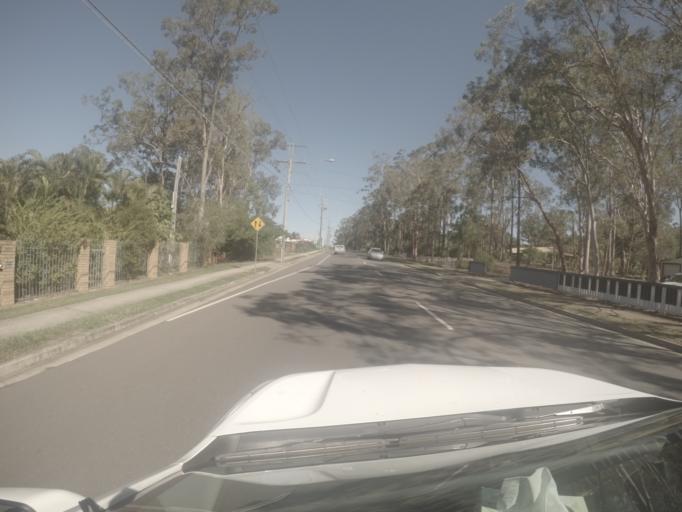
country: AU
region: Queensland
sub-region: Ipswich
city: Springfield
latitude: -27.6334
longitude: 152.9159
